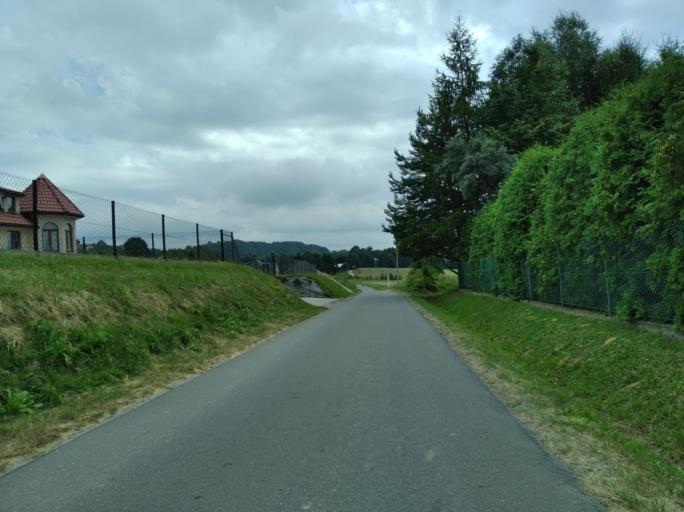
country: PL
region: Subcarpathian Voivodeship
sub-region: Powiat krosnienski
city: Odrzykon
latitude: 49.7414
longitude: 21.7581
